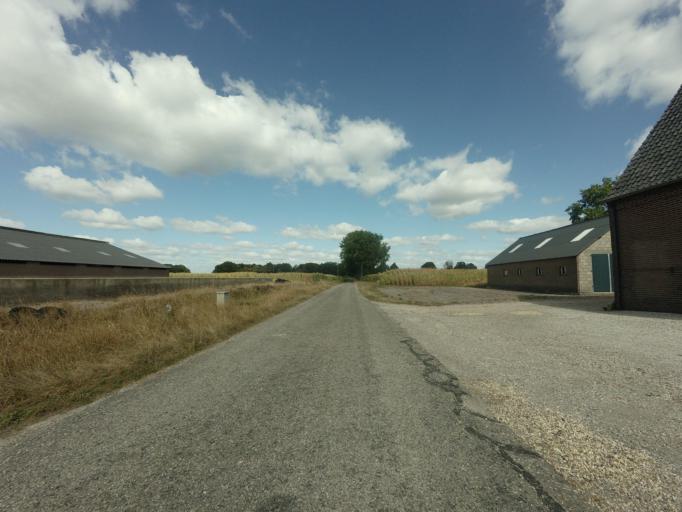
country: NL
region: North Brabant
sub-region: Gemeente Landerd
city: Schaijk
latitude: 51.7352
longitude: 5.6155
